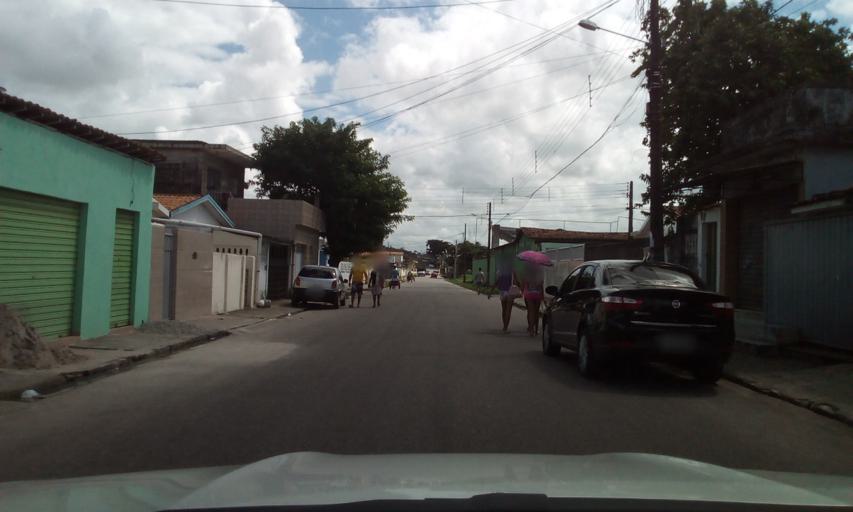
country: BR
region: Paraiba
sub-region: Bayeux
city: Bayeux
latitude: -7.1346
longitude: -34.9251
